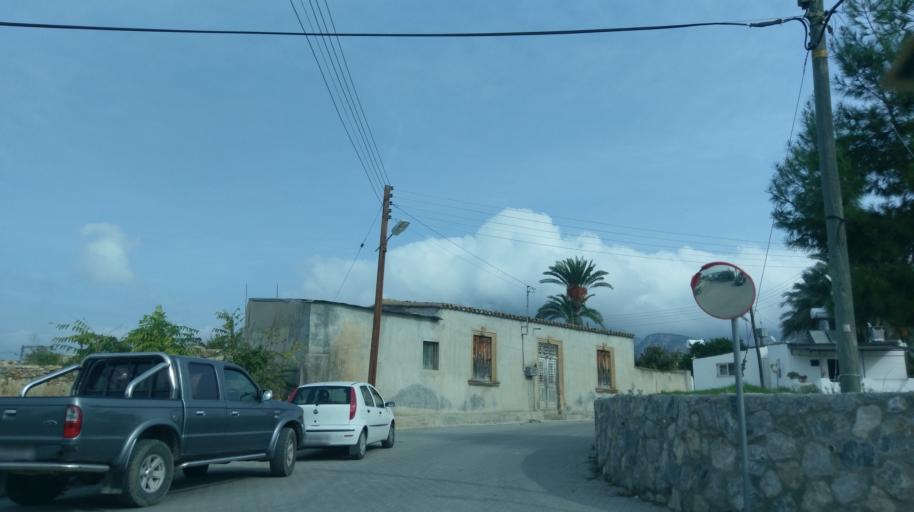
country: CY
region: Keryneia
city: Lapithos
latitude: 35.3011
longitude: 33.1075
